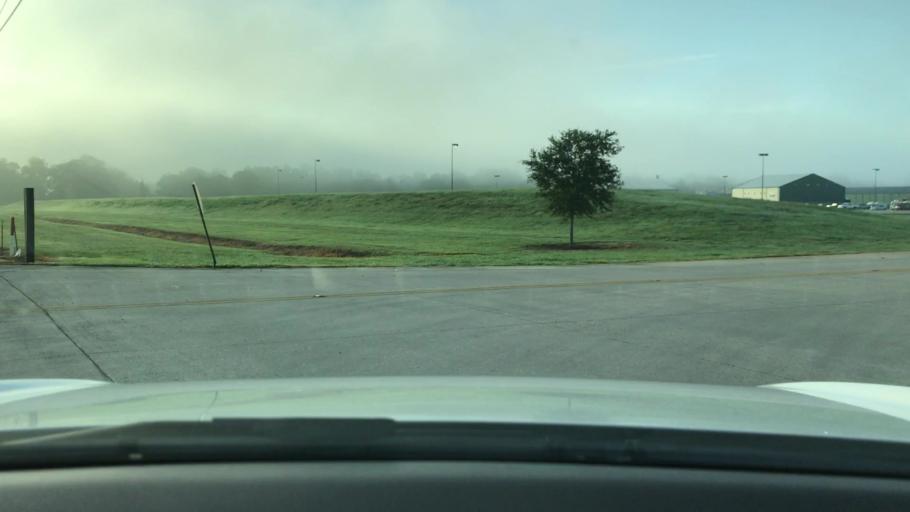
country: US
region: Louisiana
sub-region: Iberville Parish
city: Saint Gabriel
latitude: 30.2709
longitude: -91.1479
